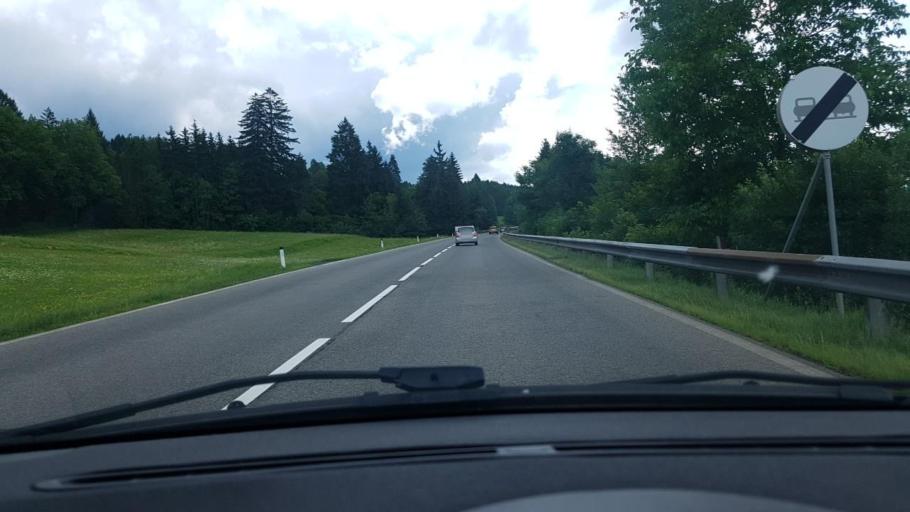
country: AT
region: Carinthia
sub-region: Politischer Bezirk Villach Land
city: Stockenboi
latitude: 46.6225
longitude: 13.4949
